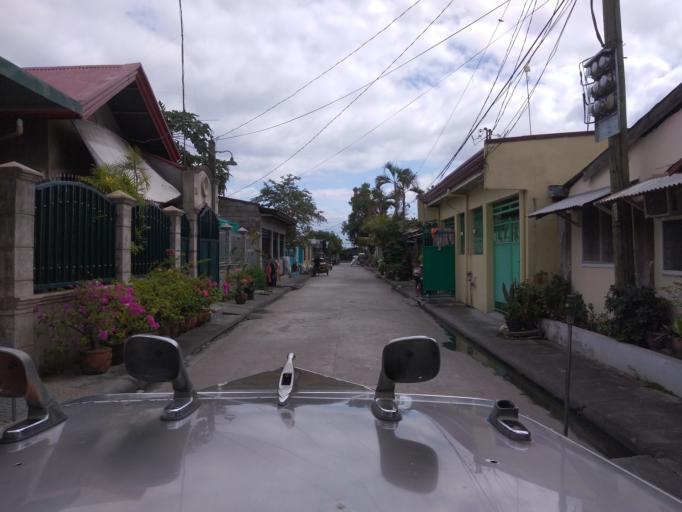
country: PH
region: Central Luzon
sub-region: Province of Pampanga
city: Pandacaqui
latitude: 15.1748
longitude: 120.6500
